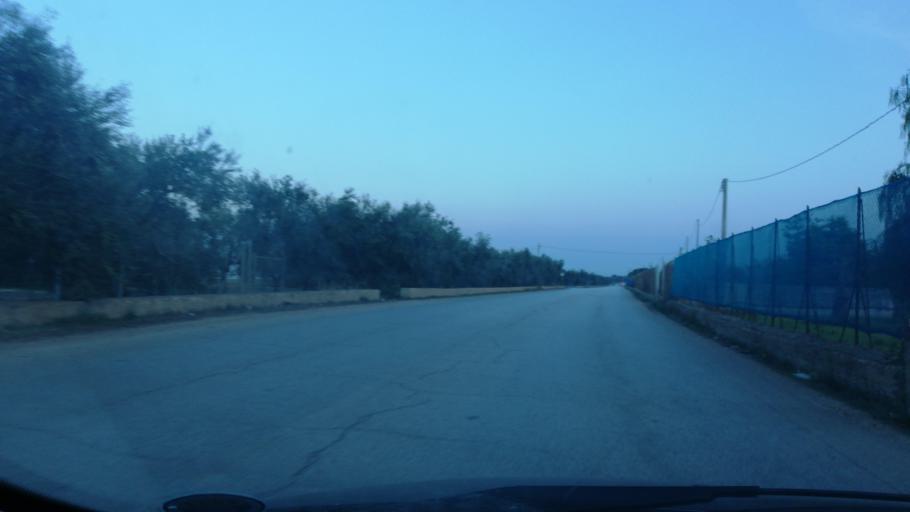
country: IT
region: Apulia
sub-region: Provincia di Bari
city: Bitonto
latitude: 41.1314
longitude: 16.7063
